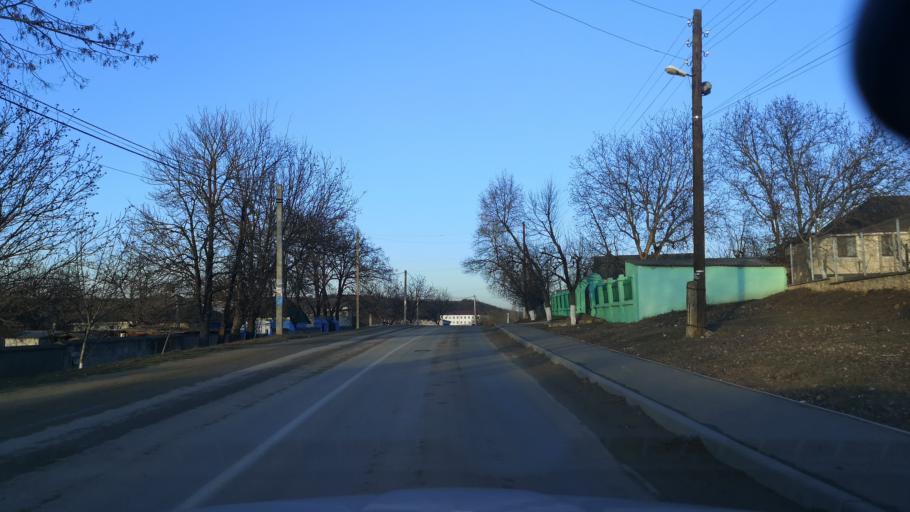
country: MD
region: Orhei
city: Orhei
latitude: 47.3076
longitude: 28.9300
